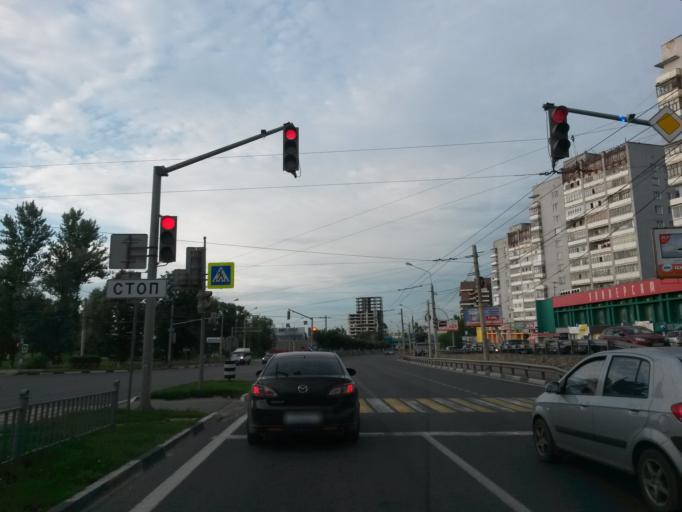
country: RU
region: Jaroslavl
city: Yaroslavl
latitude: 57.5895
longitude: 39.8594
